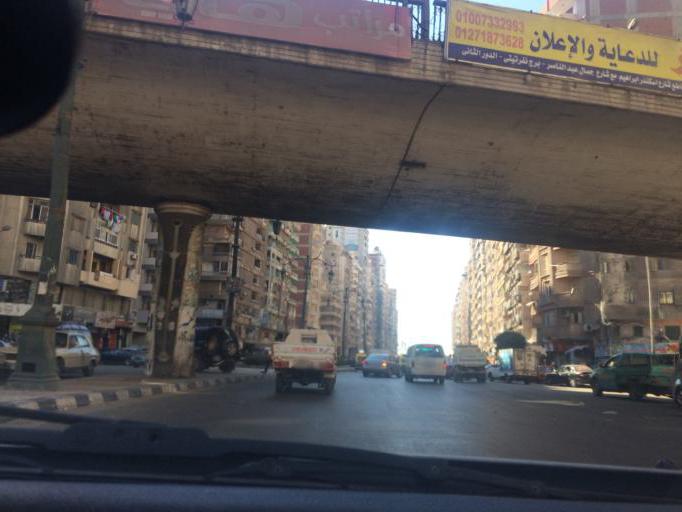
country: EG
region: Alexandria
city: Alexandria
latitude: 31.2674
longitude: 30.0004
